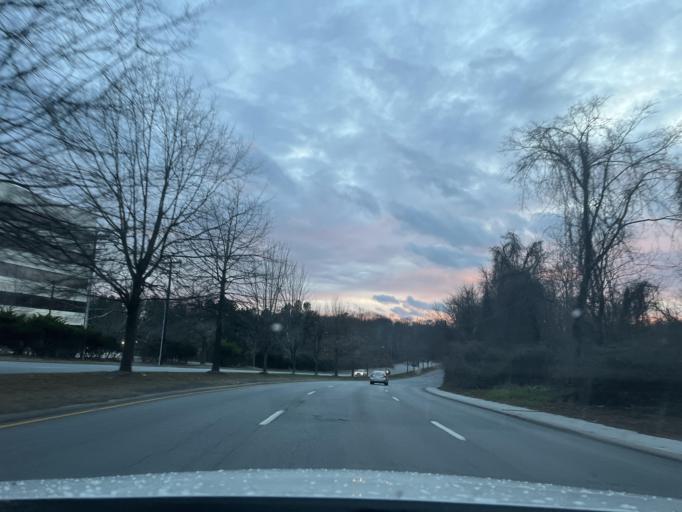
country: US
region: North Carolina
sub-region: Guilford County
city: Greensboro
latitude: 36.0502
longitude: -79.8449
